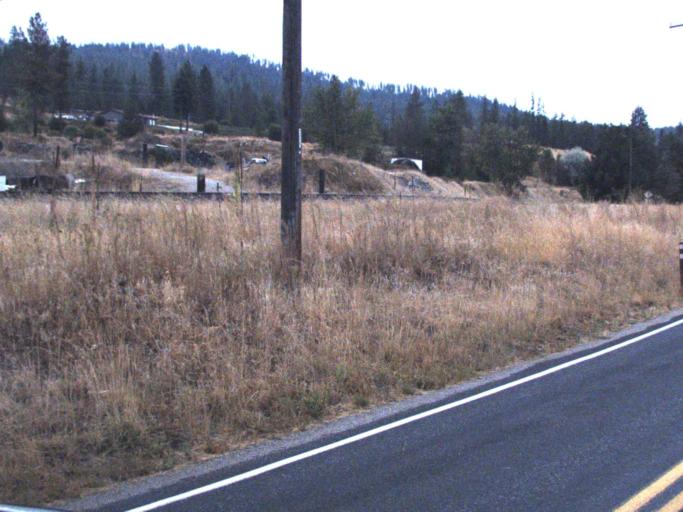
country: US
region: Washington
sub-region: Stevens County
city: Chewelah
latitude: 48.1468
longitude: -117.7279
